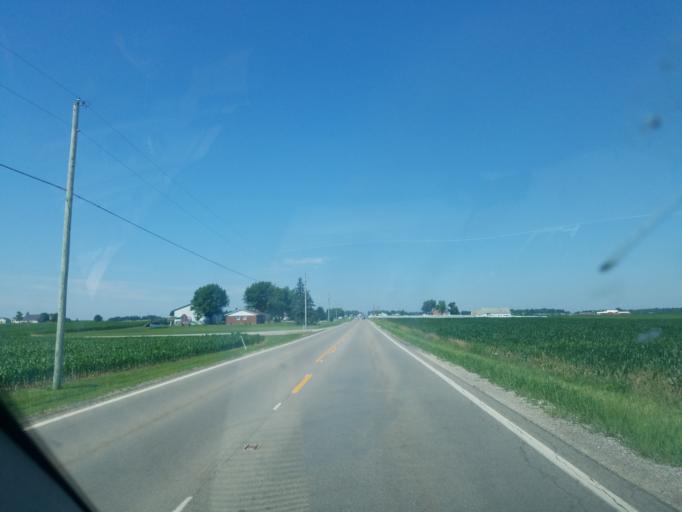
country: US
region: Ohio
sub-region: Auglaize County
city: Minster
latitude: 40.4076
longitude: -84.4494
